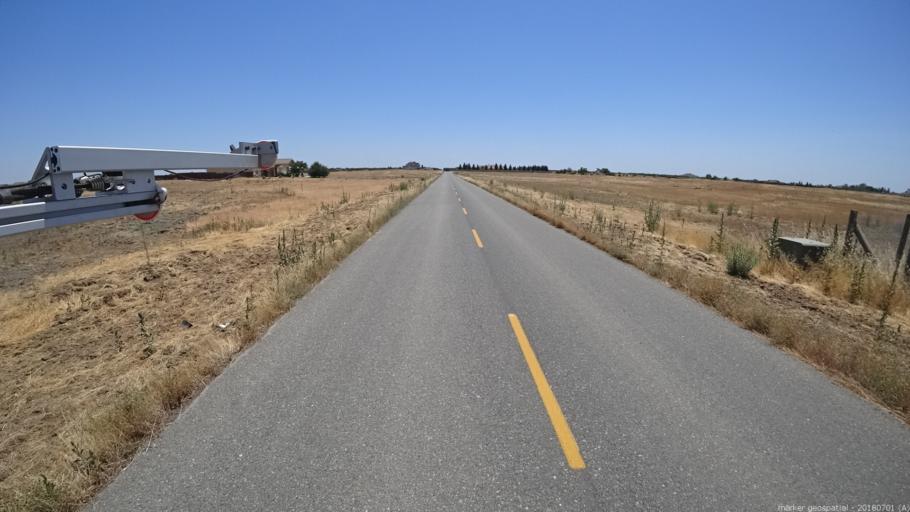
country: US
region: California
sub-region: Madera County
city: Madera Acres
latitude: 37.0606
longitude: -120.0158
